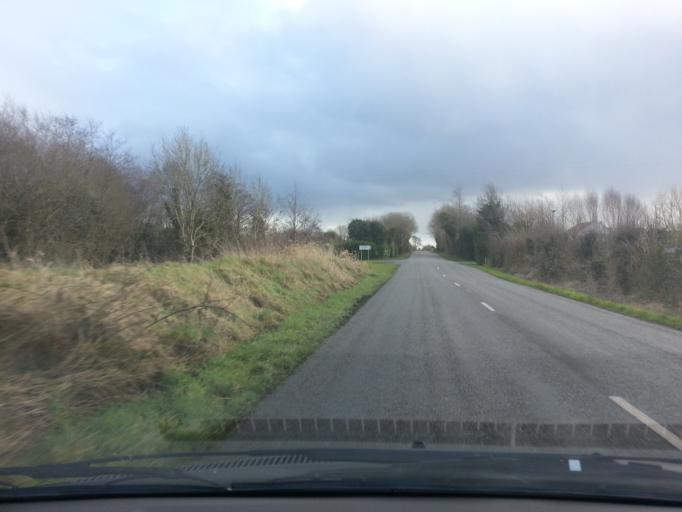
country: GB
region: Northern Ireland
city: Lisnaskea
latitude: 54.2758
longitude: -7.5043
